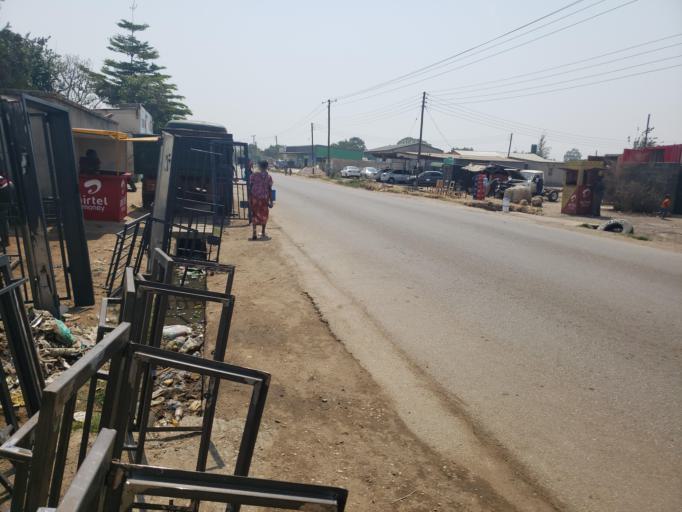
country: ZM
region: Lusaka
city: Lusaka
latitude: -15.4469
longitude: 28.2443
